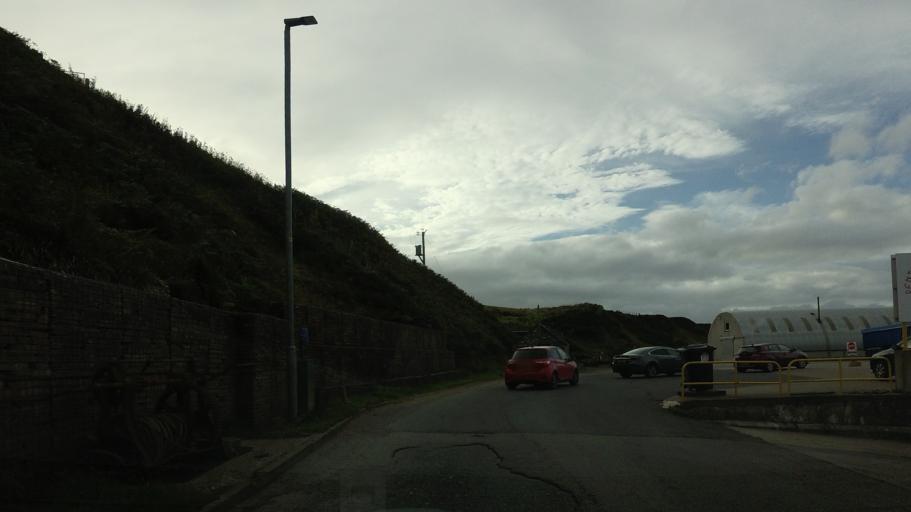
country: GB
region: Scotland
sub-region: Highland
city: Wick
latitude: 58.6379
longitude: -3.1618
